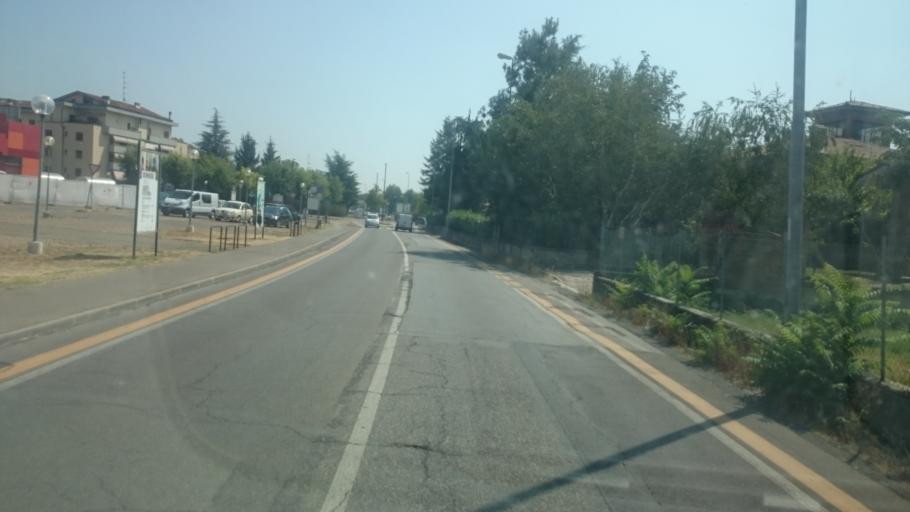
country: IT
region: Emilia-Romagna
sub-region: Provincia di Reggio Emilia
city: Reggio nell'Emilia
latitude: 44.6823
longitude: 10.6621
